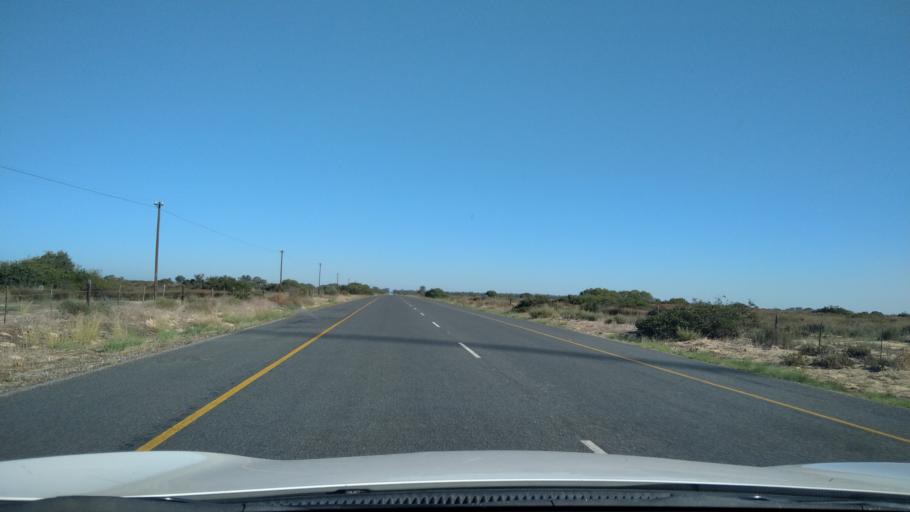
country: ZA
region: Western Cape
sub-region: West Coast District Municipality
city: Moorreesburg
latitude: -33.0839
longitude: 18.3948
